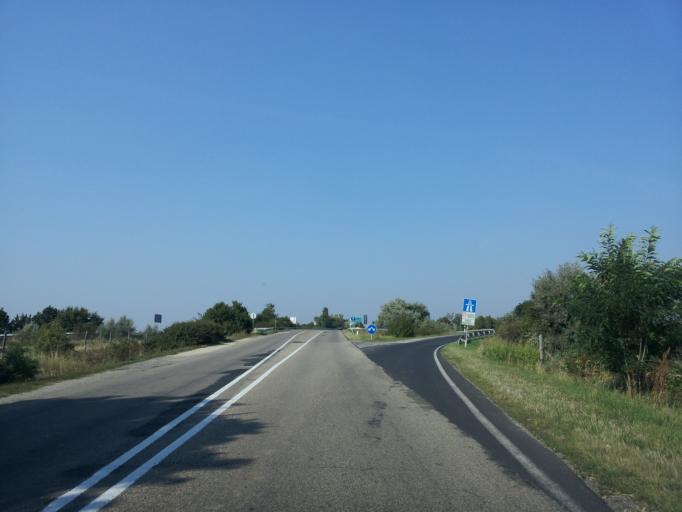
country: HU
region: Fejer
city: Polgardi
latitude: 47.0390
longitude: 18.2943
